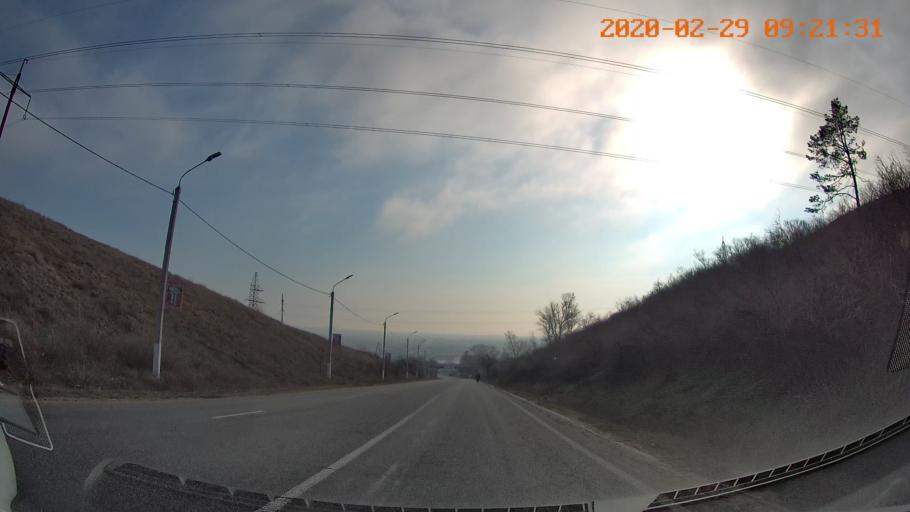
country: MD
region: Telenesti
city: Pervomaisc
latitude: 46.7385
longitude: 29.9596
